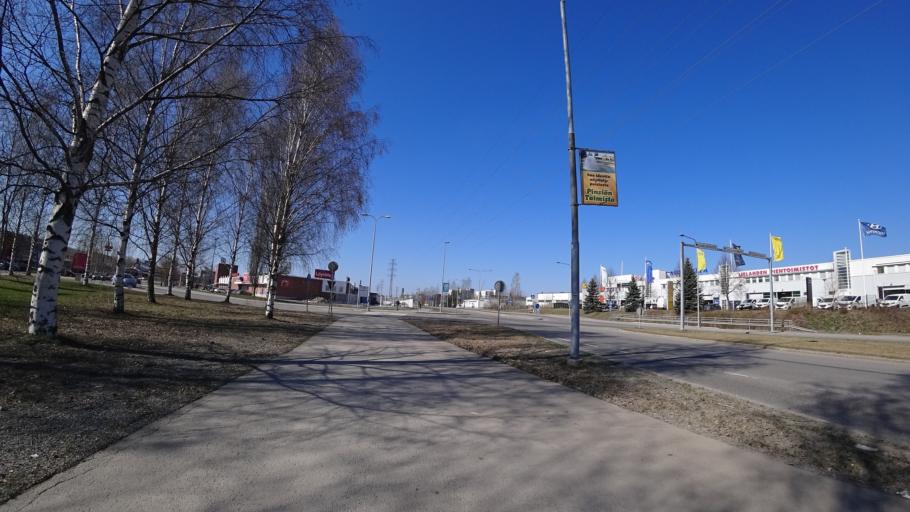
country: FI
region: Pirkanmaa
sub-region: Tampere
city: Pirkkala
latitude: 61.5140
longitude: 23.6732
